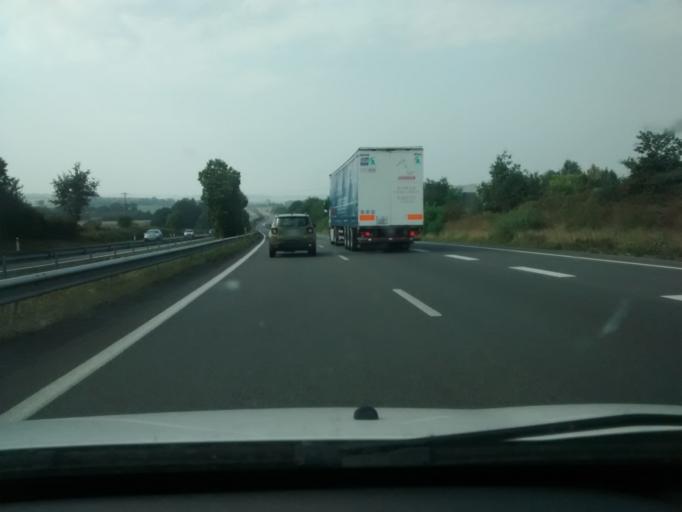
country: FR
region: Brittany
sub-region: Departement d'Ille-et-Vilaine
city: Crevin
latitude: 47.9267
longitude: -1.6758
